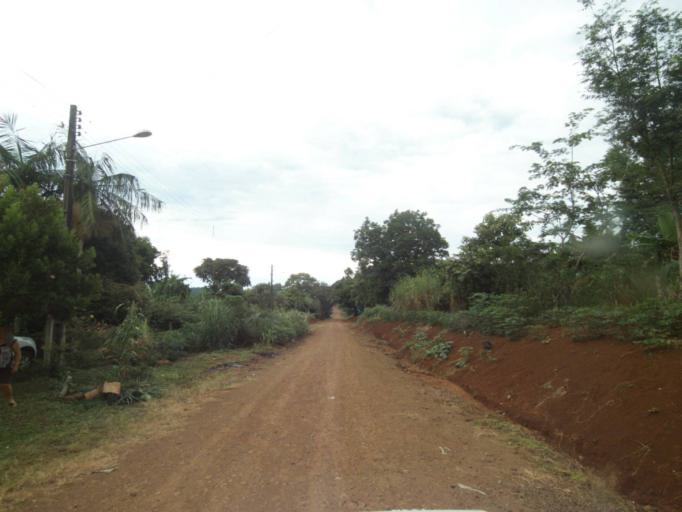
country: BR
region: Parana
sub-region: Guaraniacu
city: Guaraniacu
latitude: -24.9209
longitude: -52.9395
